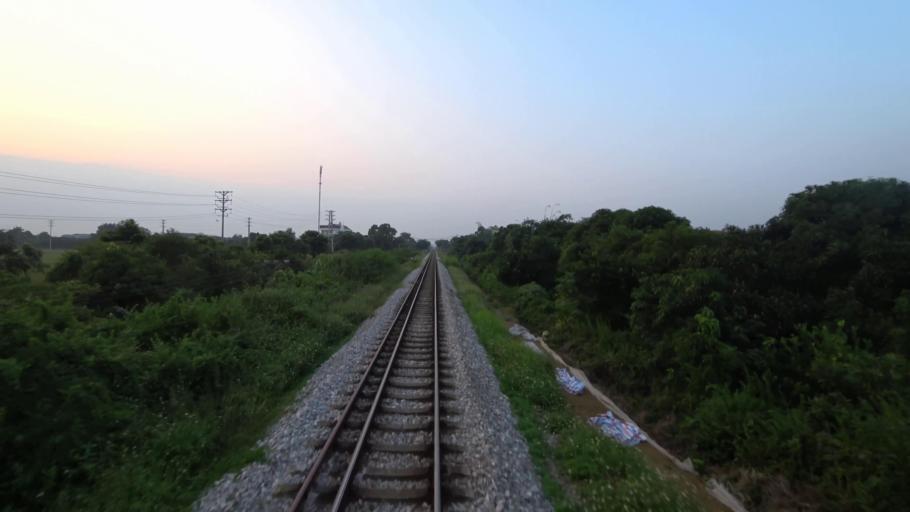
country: VN
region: Ha Noi
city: Dong Anh
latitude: 21.1258
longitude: 105.8808
